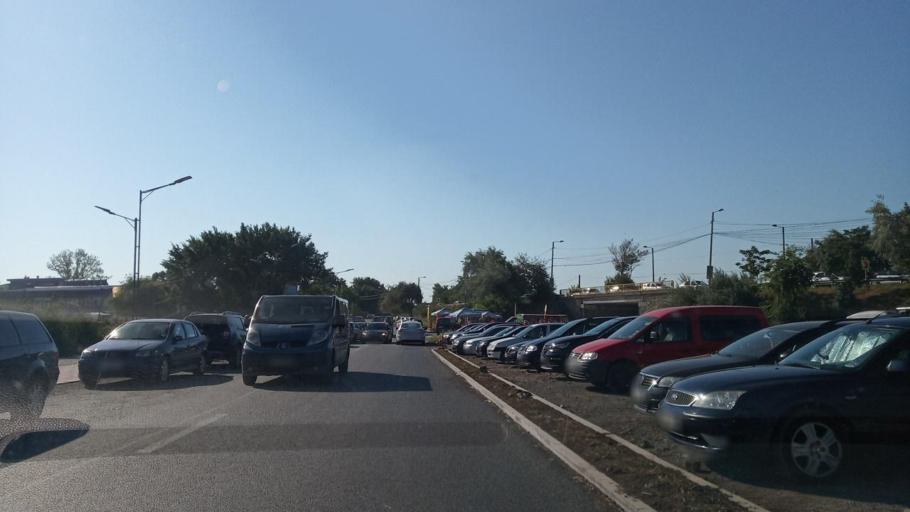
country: RO
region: Constanta
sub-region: Oras Eforie
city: Eforie Nord
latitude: 44.0587
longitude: 28.6371
